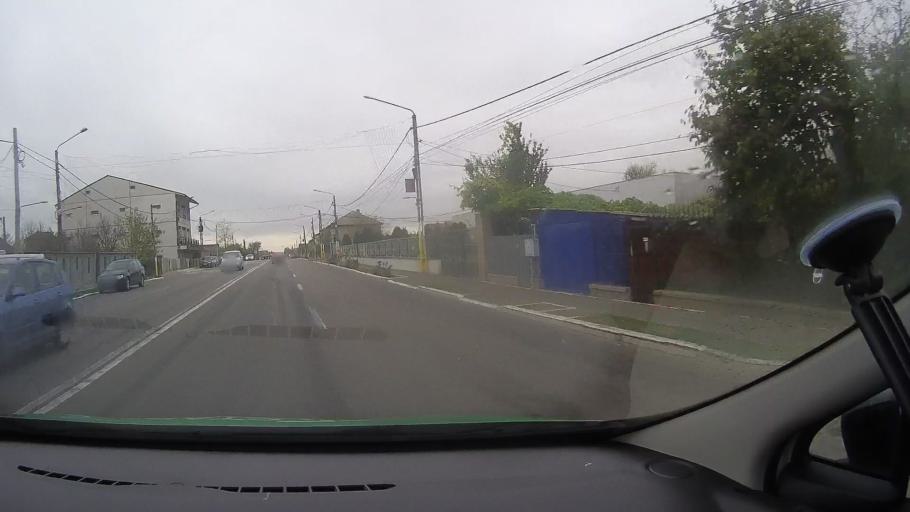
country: RO
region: Constanta
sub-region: Comuna Valu lui Traian
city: Valu lui Traian
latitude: 44.1662
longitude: 28.4624
